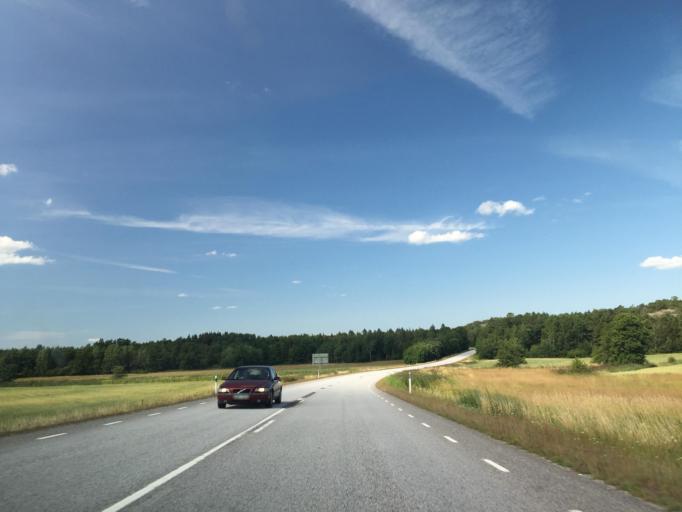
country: SE
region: Vaestra Goetaland
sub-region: Tanums Kommun
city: Tanumshede
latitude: 58.8129
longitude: 11.2632
